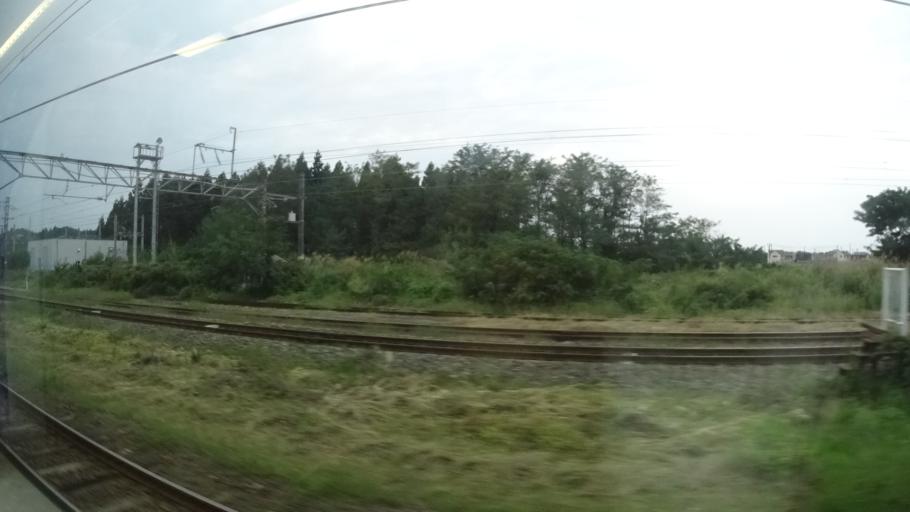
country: JP
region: Niigata
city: Murakami
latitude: 38.2186
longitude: 139.4633
